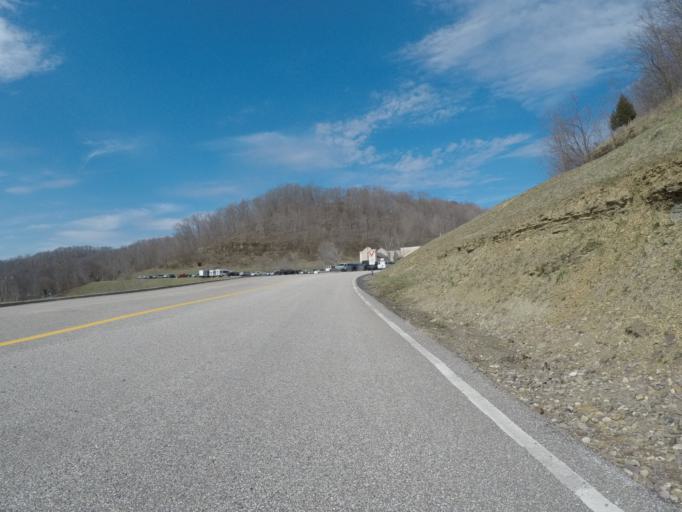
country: US
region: West Virginia
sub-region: Cabell County
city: Huntington
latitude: 38.3968
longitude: -82.4569
